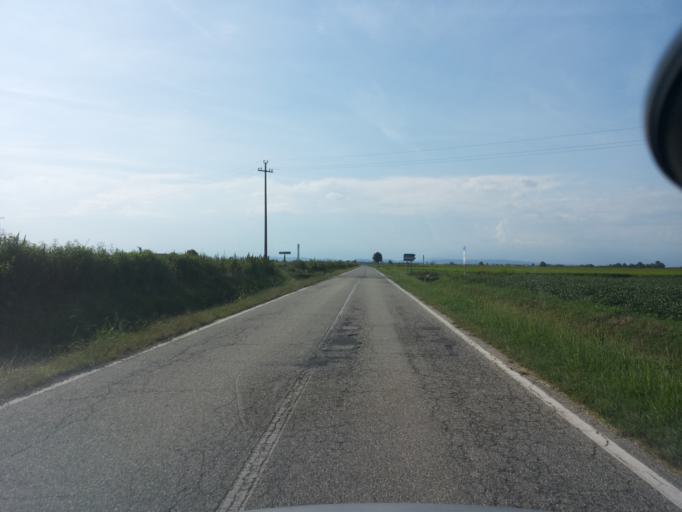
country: IT
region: Piedmont
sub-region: Provincia di Vercelli
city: Salasco
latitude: 45.3011
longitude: 8.2645
